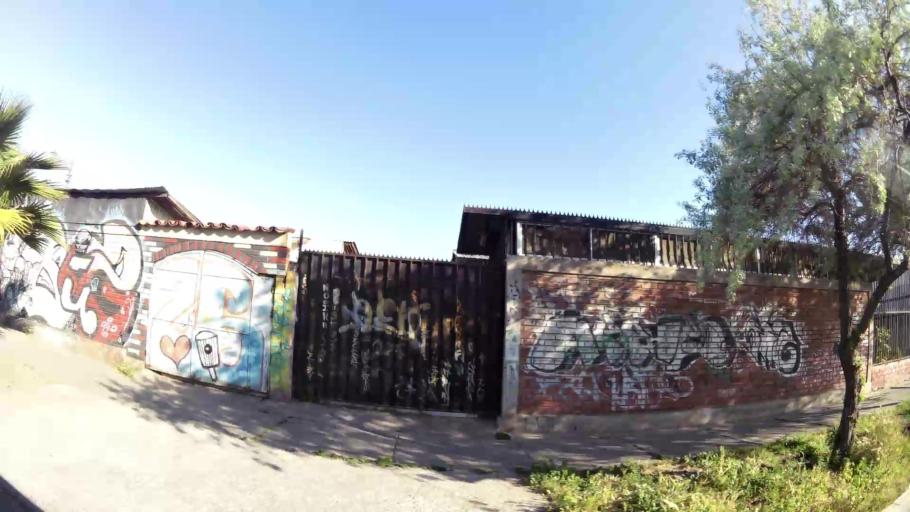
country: CL
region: Santiago Metropolitan
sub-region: Provincia de Santiago
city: La Pintana
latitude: -33.5532
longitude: -70.6280
